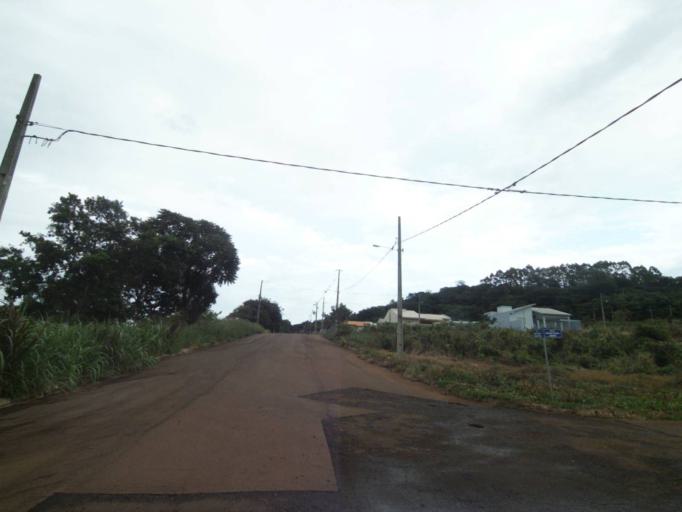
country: BR
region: Parana
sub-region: Guaraniacu
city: Guaraniacu
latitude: -25.1016
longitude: -52.8860
